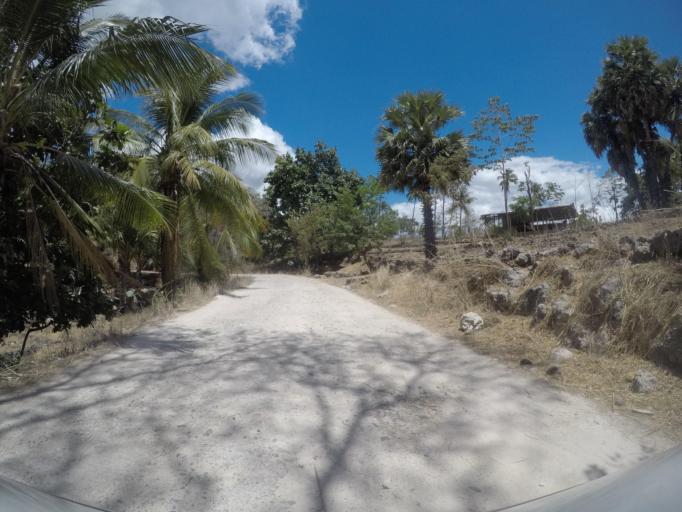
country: TL
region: Baucau
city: Baucau
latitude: -8.4836
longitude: 126.6326
